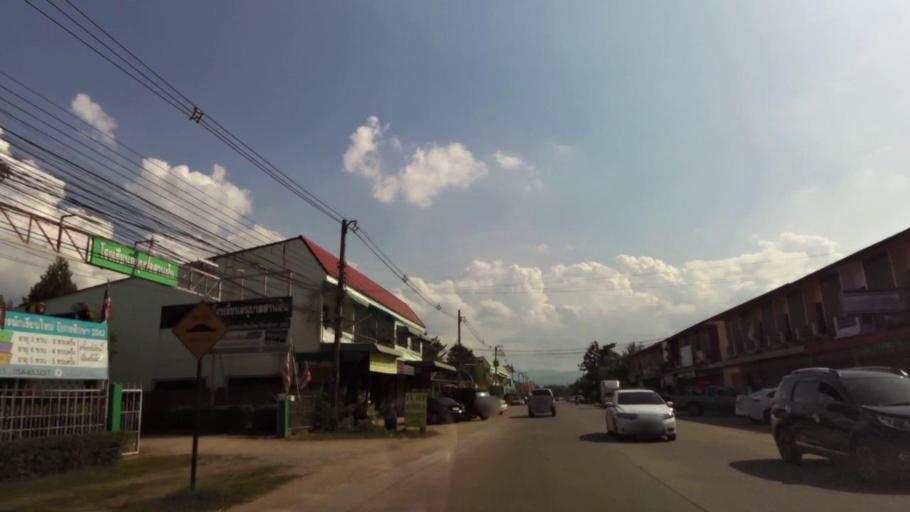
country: TH
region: Phrae
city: Phrae
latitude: 18.1233
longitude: 100.1528
